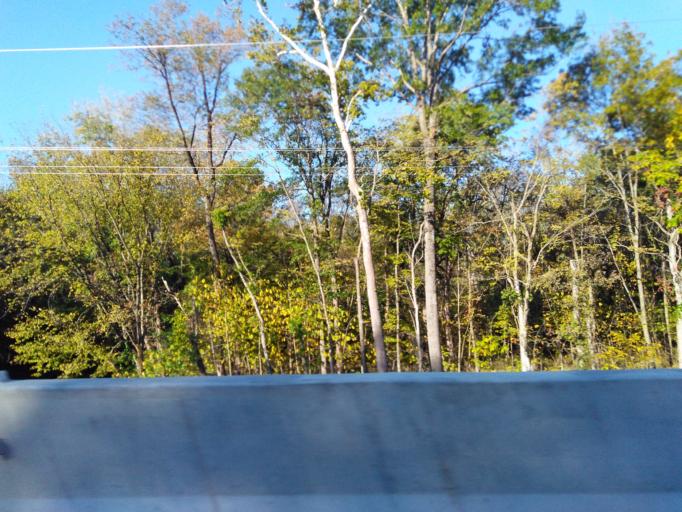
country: US
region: Illinois
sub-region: Madison County
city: Saint Jacob
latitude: 38.7249
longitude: -89.8012
